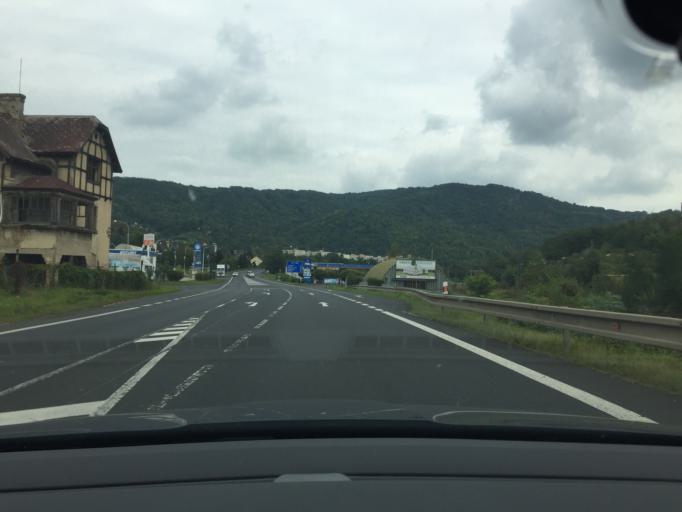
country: CZ
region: Ustecky
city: Velke Brezno
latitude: 50.6744
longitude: 14.1090
